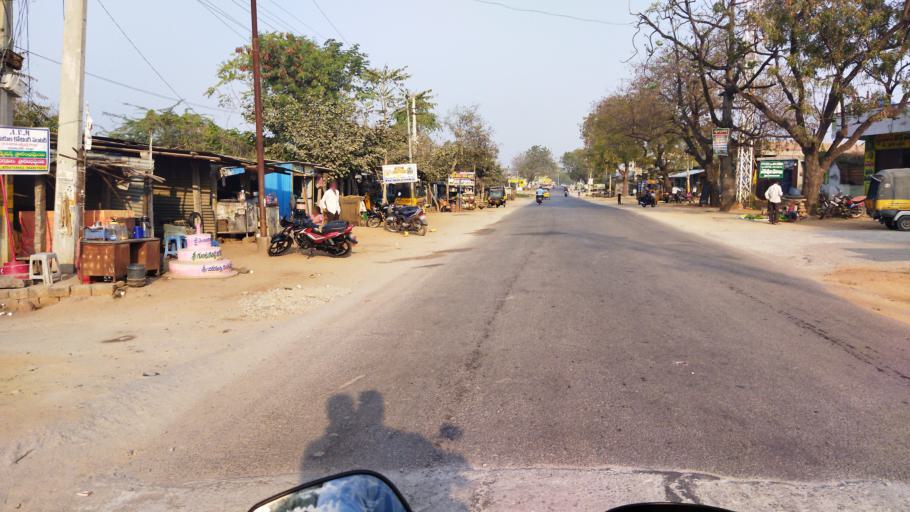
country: IN
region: Telangana
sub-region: Nalgonda
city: Nalgonda
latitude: 17.2346
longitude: 79.1236
